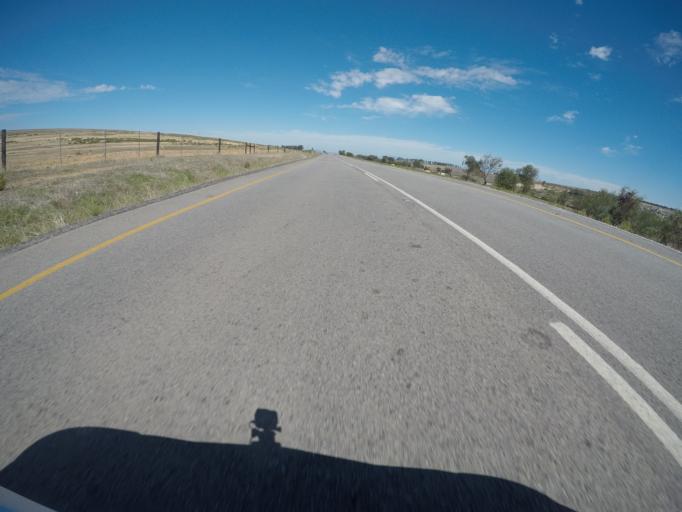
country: ZA
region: Western Cape
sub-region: West Coast District Municipality
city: Malmesbury
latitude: -33.4939
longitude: 18.6818
